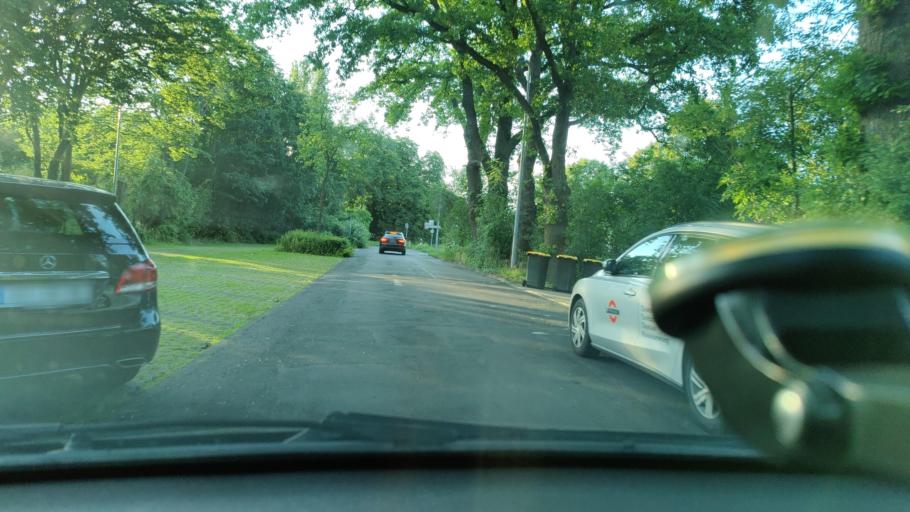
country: DE
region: North Rhine-Westphalia
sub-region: Regierungsbezirk Dusseldorf
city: Kamp-Lintfort
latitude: 51.5040
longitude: 6.5205
